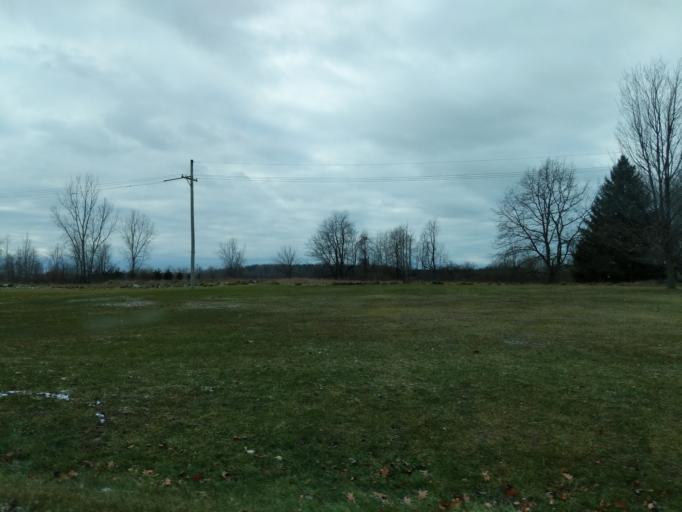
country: US
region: Michigan
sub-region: Lapeer County
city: North Branch
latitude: 43.3229
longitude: -83.1794
